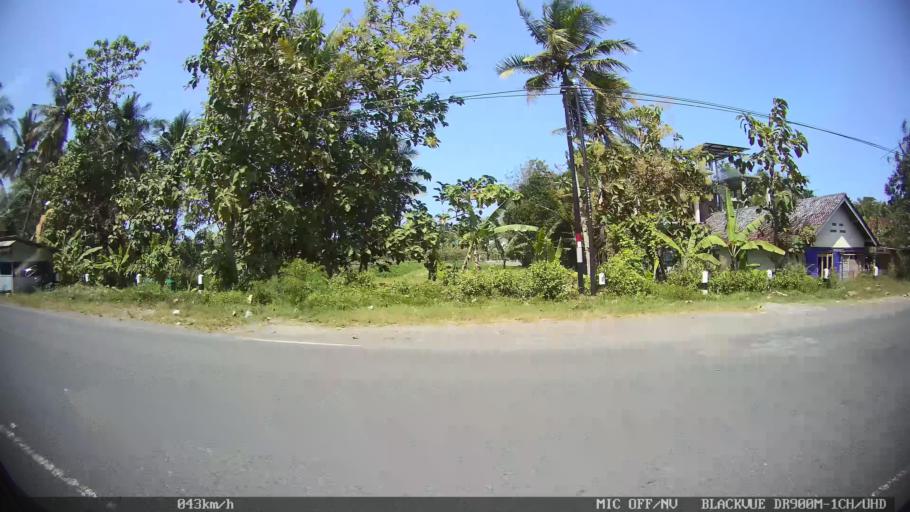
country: ID
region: Daerah Istimewa Yogyakarta
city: Srandakan
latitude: -7.8879
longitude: 110.0469
